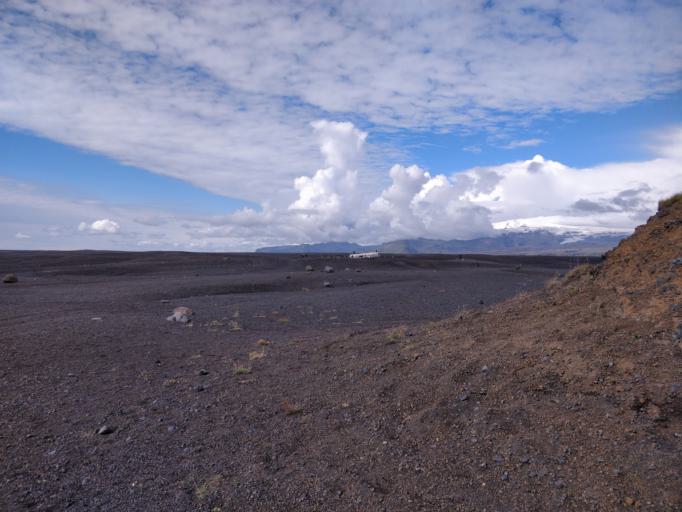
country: IS
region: South
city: Vestmannaeyjar
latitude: 63.4576
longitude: -19.3609
